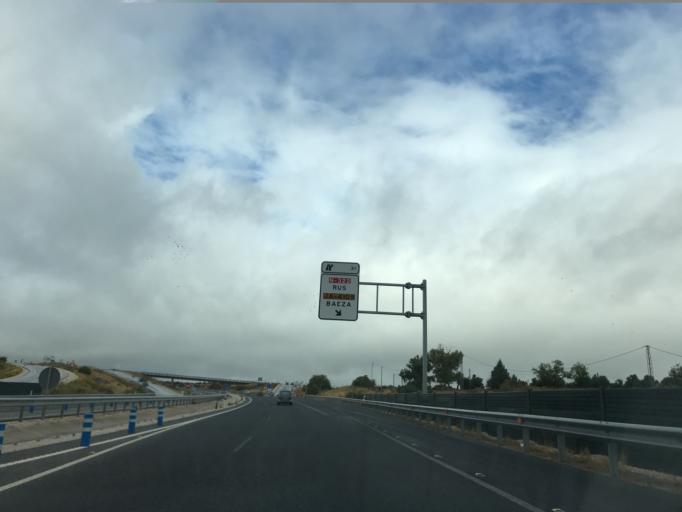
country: ES
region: Andalusia
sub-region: Provincia de Jaen
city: Ubeda
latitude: 38.0215
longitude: -3.4155
